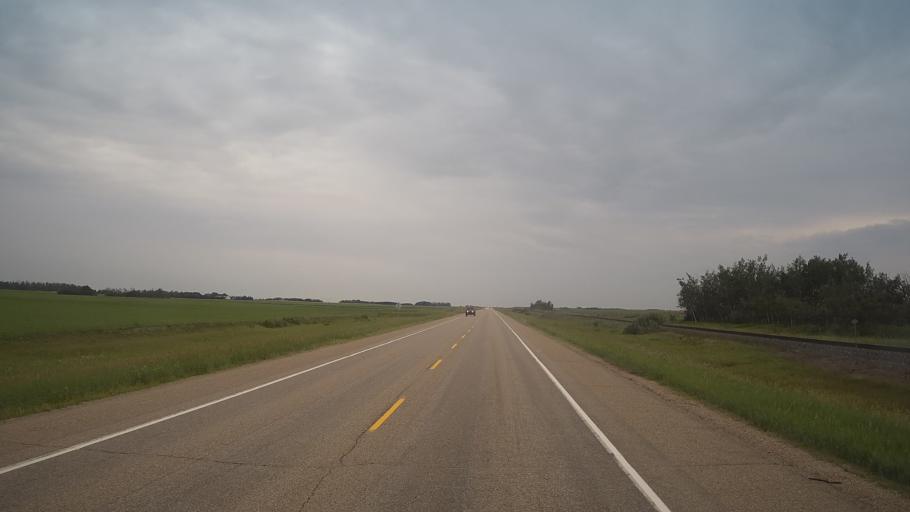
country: CA
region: Saskatchewan
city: Langham
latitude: 52.1252
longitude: -107.2938
